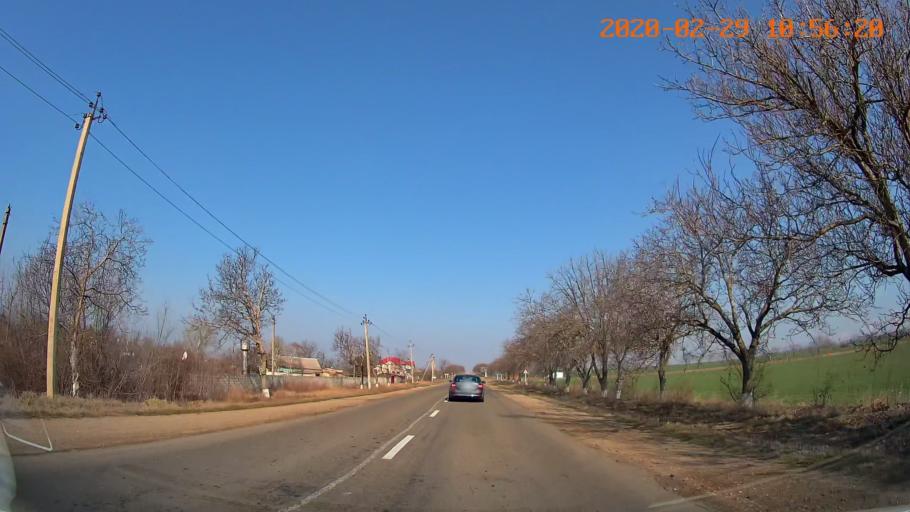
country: MD
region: Telenesti
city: Grigoriopol
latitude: 47.1446
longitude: 29.3248
